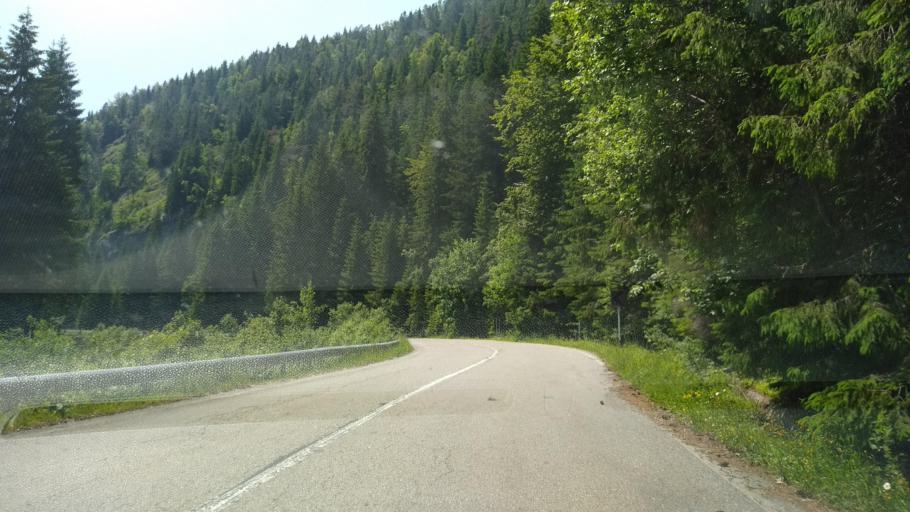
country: RO
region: Gorj
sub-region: Comuna Tismana
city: Sohodol
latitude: 45.2679
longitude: 22.8817
